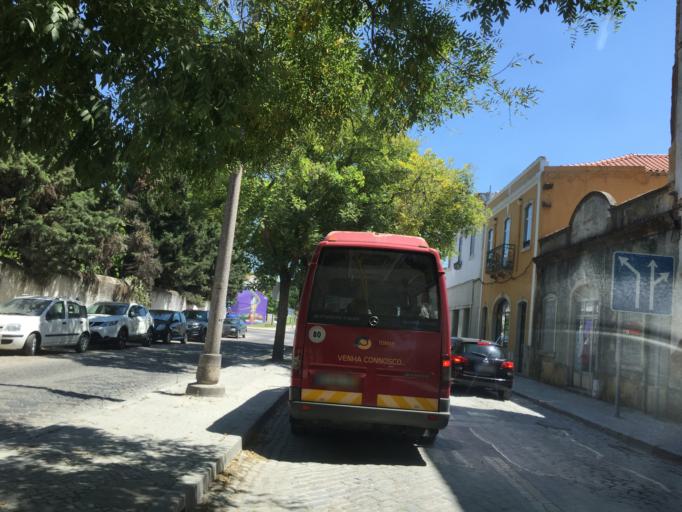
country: PT
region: Santarem
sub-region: Tomar
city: Tomar
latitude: 39.6000
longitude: -8.4120
